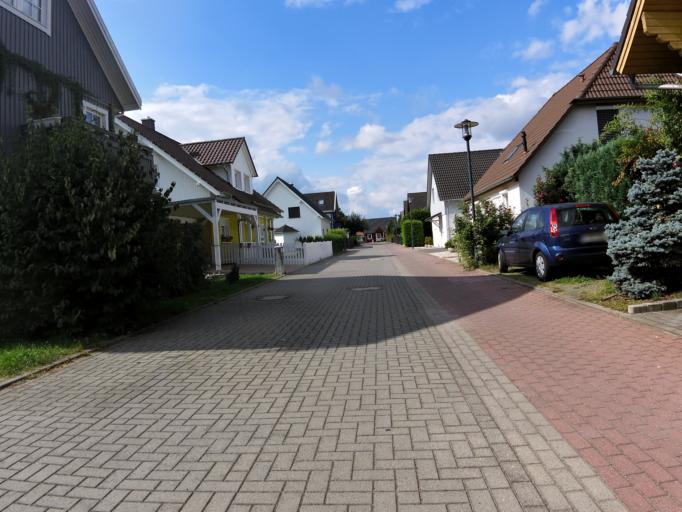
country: DE
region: Saxony
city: Rackwitz
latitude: 51.3918
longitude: 12.3625
